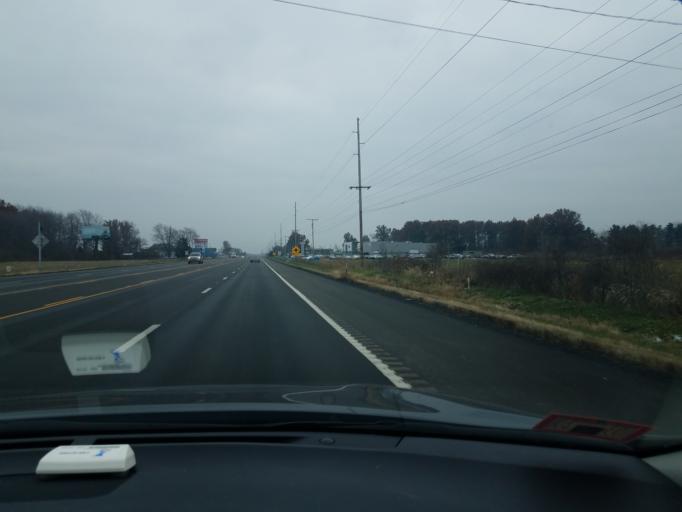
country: US
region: Ohio
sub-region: Erie County
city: Huron
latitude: 41.3810
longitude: -82.6453
